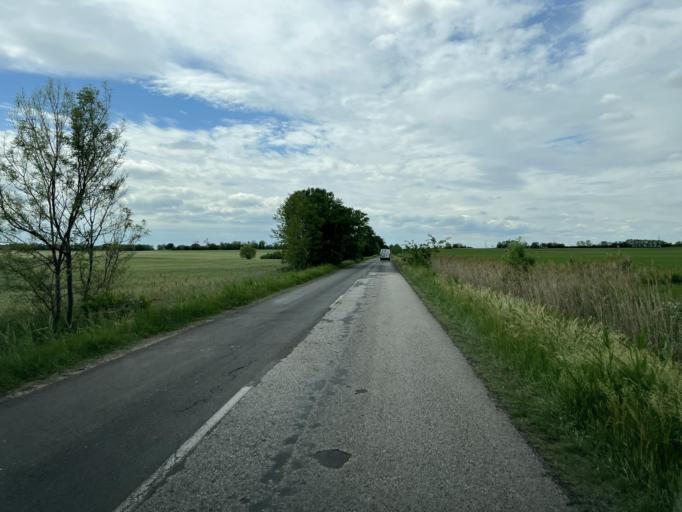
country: HU
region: Pest
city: Szentlorinckata
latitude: 47.4998
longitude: 19.7380
